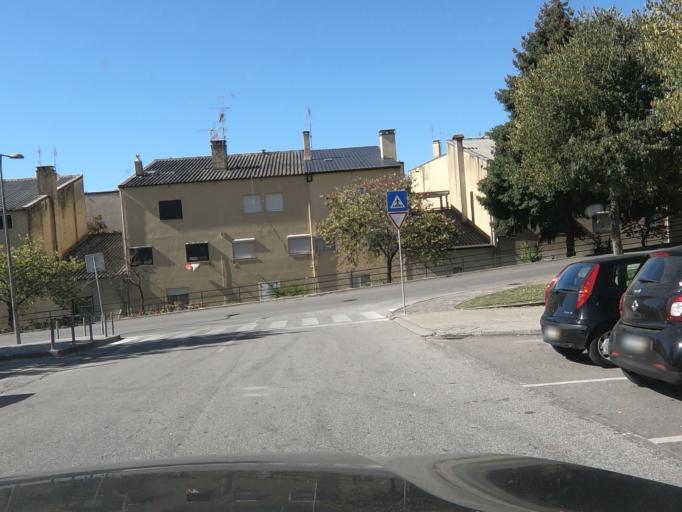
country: PT
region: Vila Real
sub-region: Vila Real
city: Vila Real
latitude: 41.3052
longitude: -7.7462
